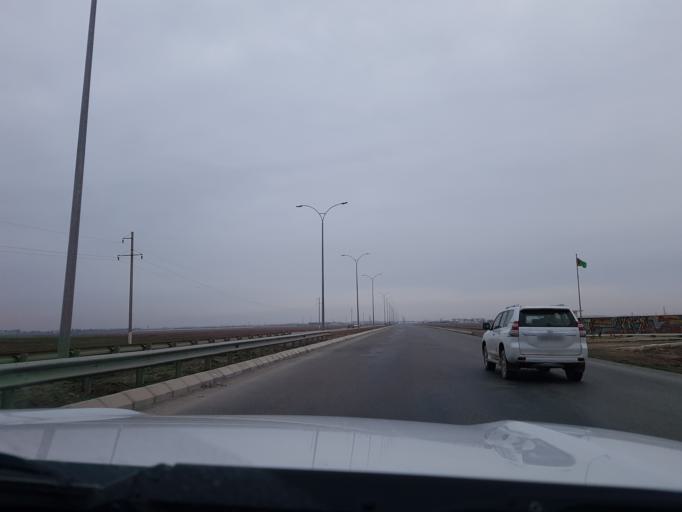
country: TM
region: Ahal
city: Tejen
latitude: 37.3717
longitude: 60.4663
